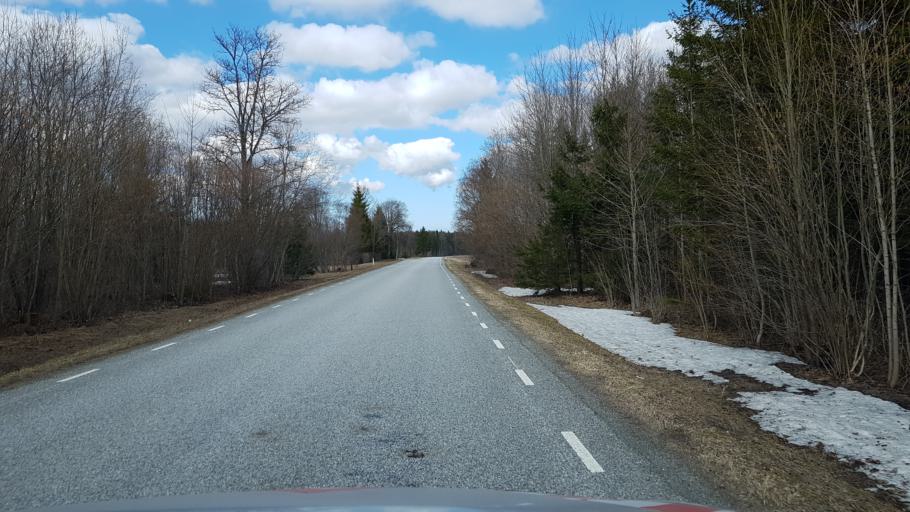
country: EE
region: Laeaene-Virumaa
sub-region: Tamsalu vald
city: Tamsalu
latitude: 59.2228
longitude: 26.1628
